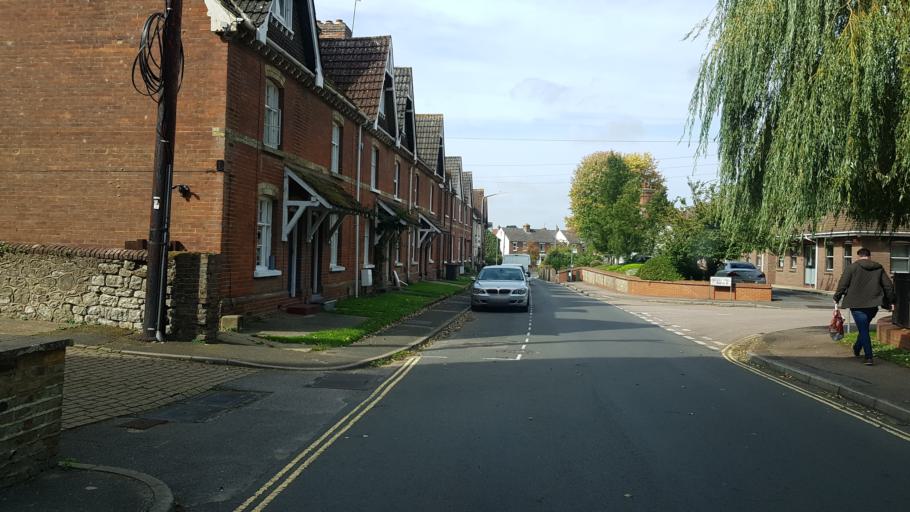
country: GB
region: England
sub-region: Kent
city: Larkfield
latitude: 51.2888
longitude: 0.4323
